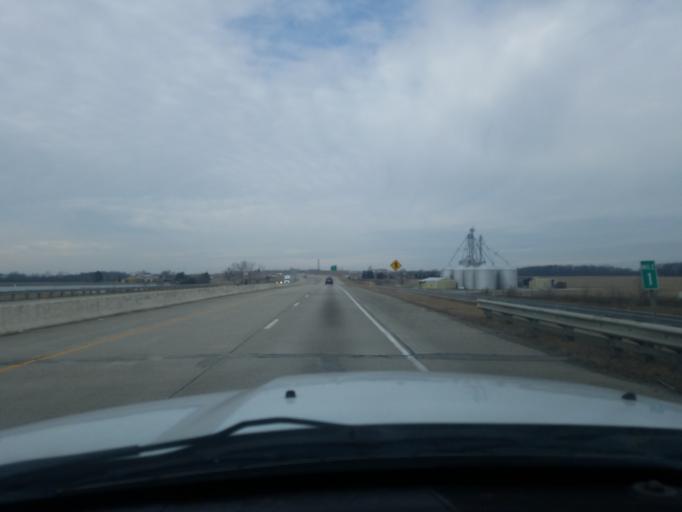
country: US
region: Indiana
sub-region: Huntington County
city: Roanoke
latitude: 40.9593
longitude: -85.2733
